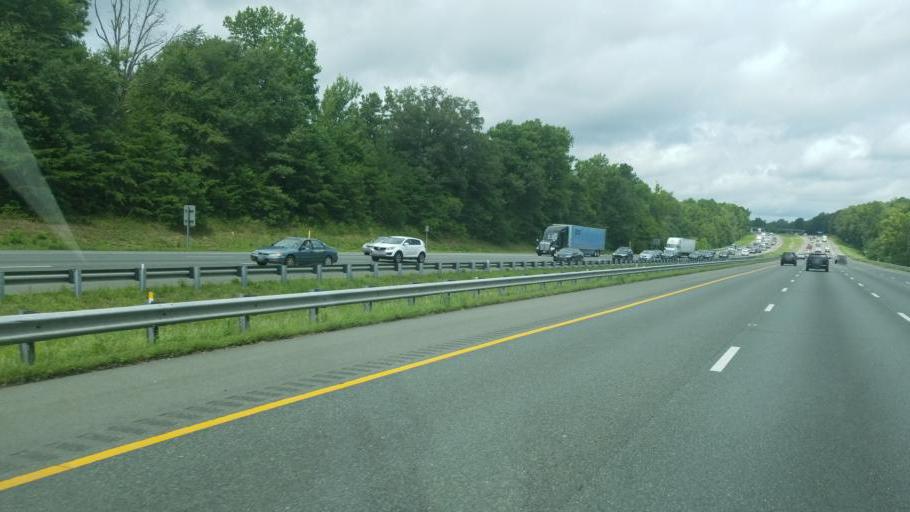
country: US
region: Virginia
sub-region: Caroline County
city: Bowling Green
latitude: 37.9845
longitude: -77.4926
